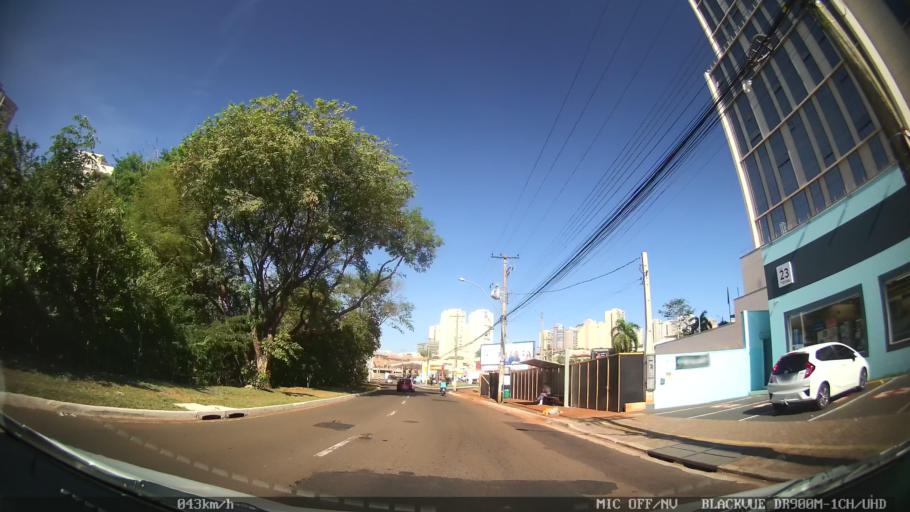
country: BR
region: Sao Paulo
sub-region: Ribeirao Preto
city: Ribeirao Preto
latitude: -21.2113
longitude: -47.7955
